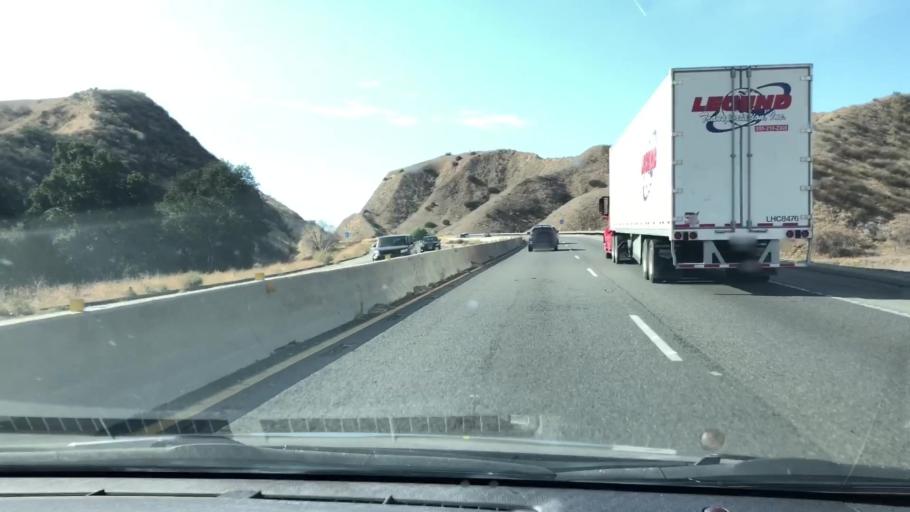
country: US
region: California
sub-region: Riverside County
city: Calimesa
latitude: 33.9462
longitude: -117.0677
